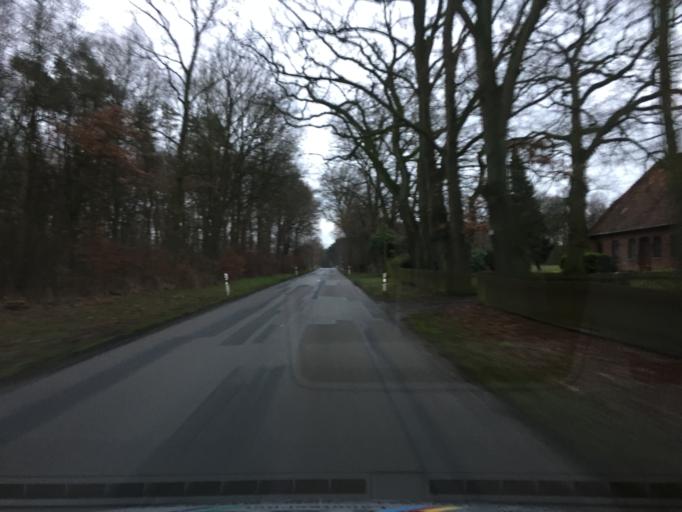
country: DE
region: Lower Saxony
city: Pennigsehl
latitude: 52.6485
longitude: 8.9981
